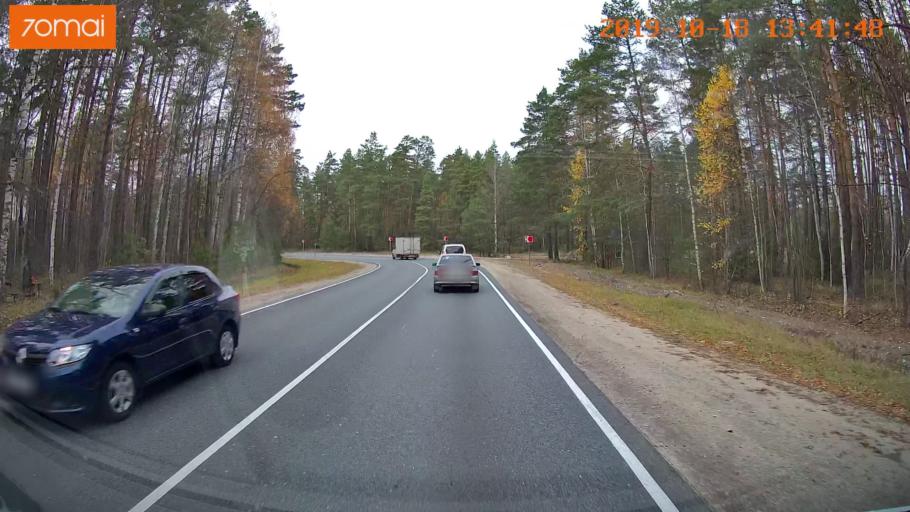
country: RU
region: Rjazan
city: Solotcha
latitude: 54.9237
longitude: 39.9970
